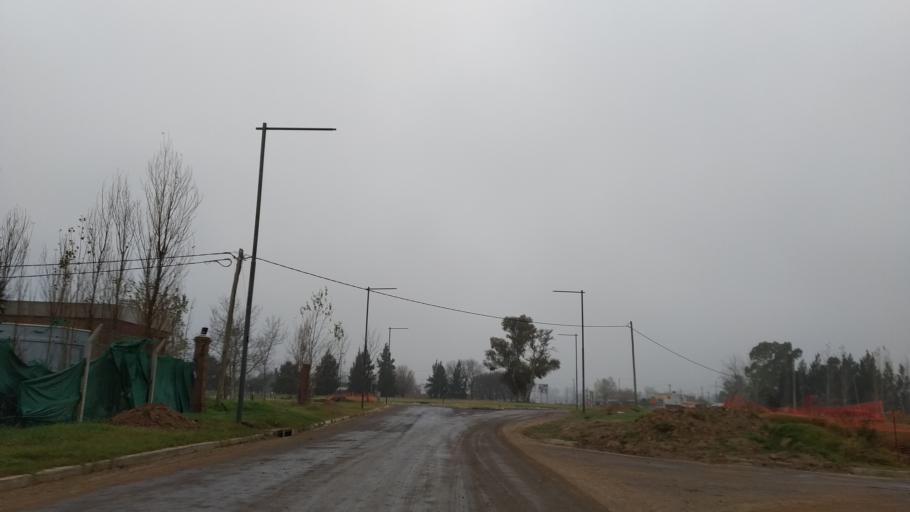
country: AR
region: Santa Fe
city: Funes
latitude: -32.9408
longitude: -60.7635
